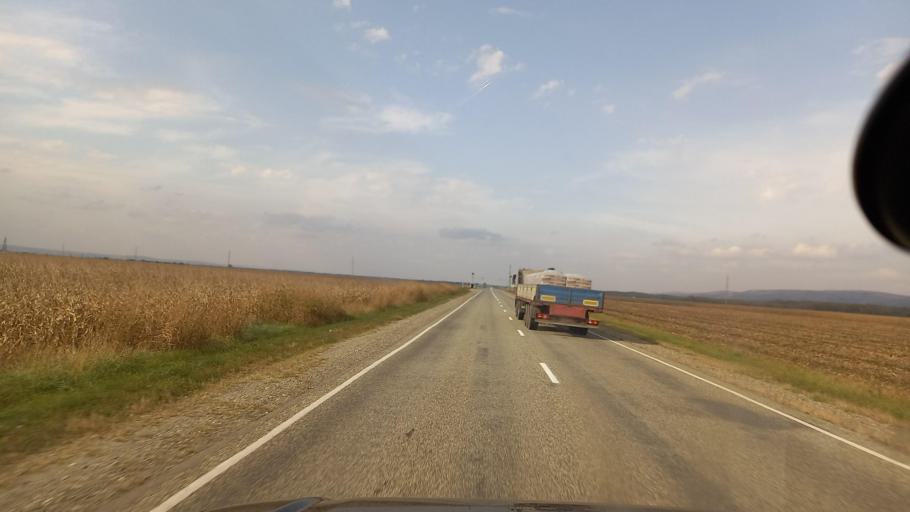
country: RU
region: Krasnodarskiy
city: Perepravnaya
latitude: 44.3189
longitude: 40.8536
